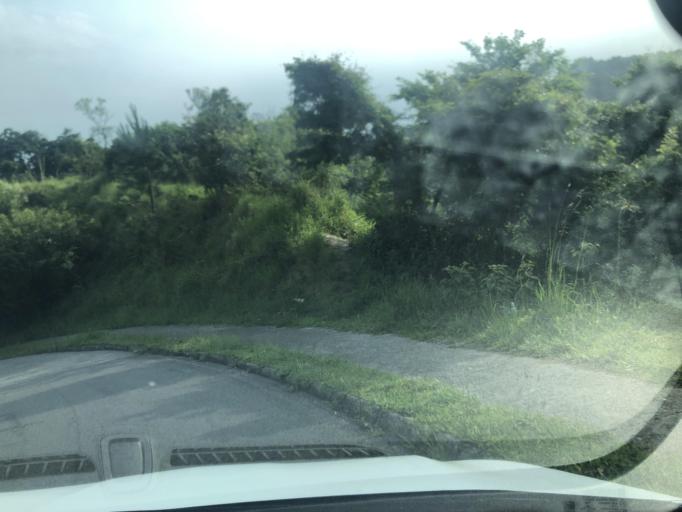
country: BR
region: Santa Catarina
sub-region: Florianopolis
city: Saco dos Limoes
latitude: -27.6027
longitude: -48.5340
